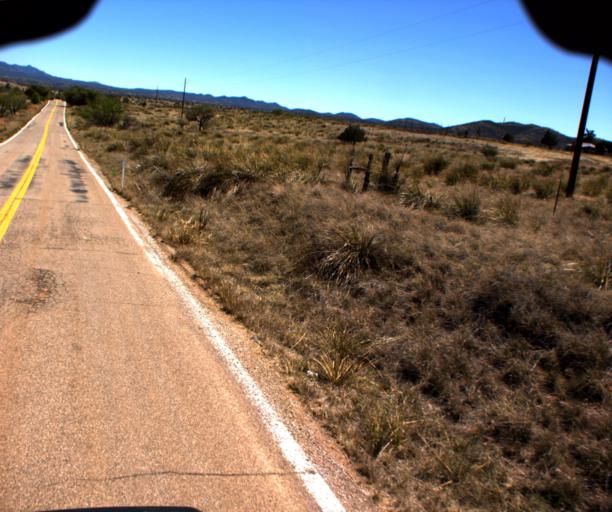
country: US
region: Arizona
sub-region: Cochise County
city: Huachuca City
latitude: 31.5855
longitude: -110.5626
